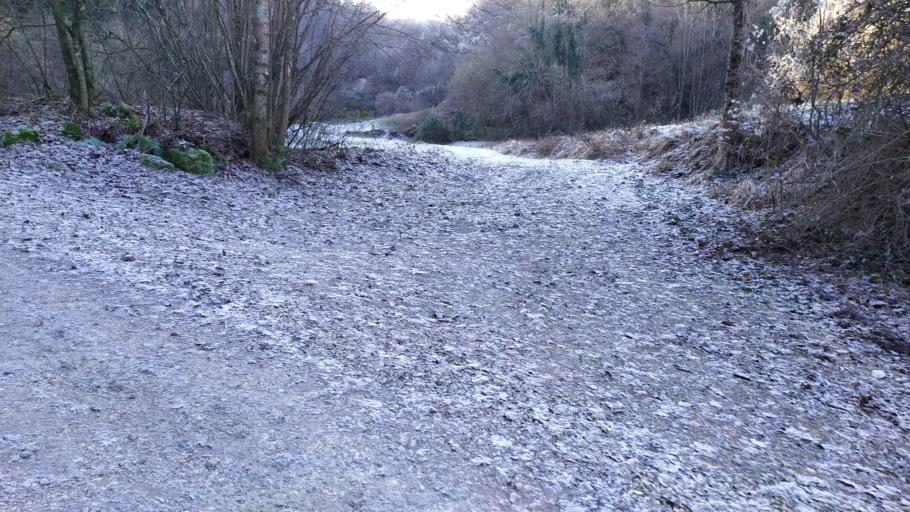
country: IT
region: Veneto
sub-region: Provincia di Vicenza
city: Monte di Malo
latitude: 45.6538
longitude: 11.3442
